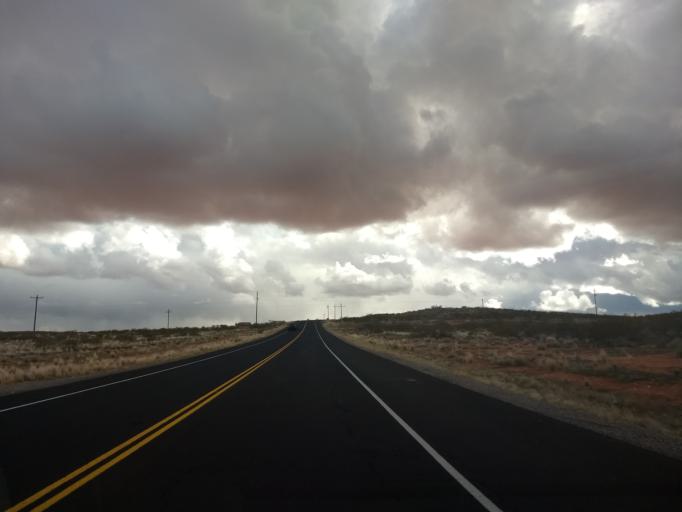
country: US
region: Utah
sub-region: Washington County
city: Hurricane
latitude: 37.1432
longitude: -113.3897
